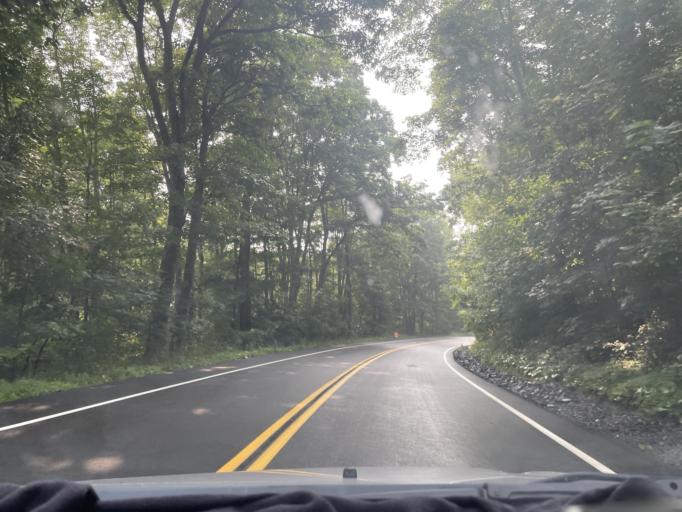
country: US
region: Maryland
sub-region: Garrett County
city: Mountain Lake Park
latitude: 39.3047
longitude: -79.3995
